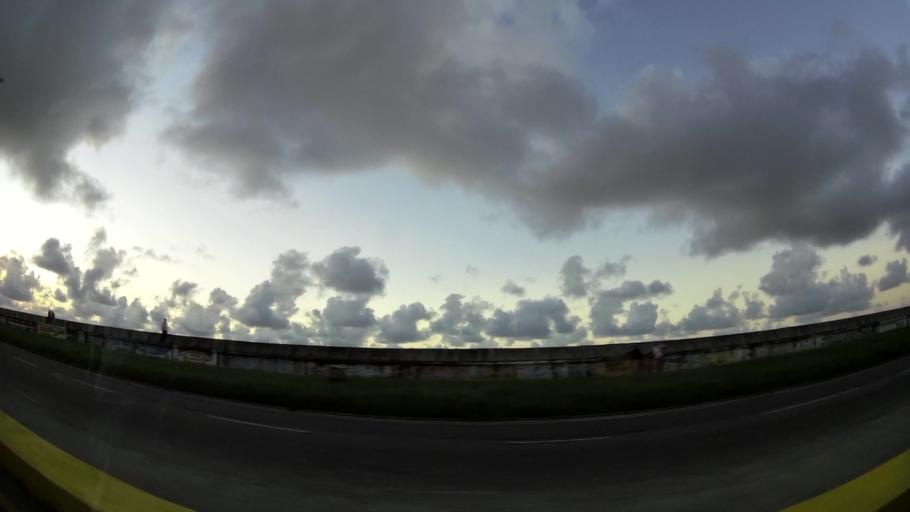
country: GY
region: Demerara-Mahaica
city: Georgetown
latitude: 6.8257
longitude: -58.1323
